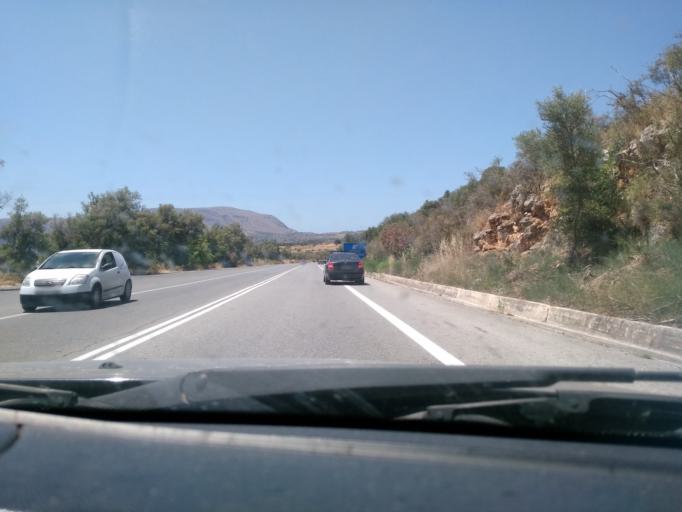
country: GR
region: Crete
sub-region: Nomos Chanias
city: Kalivai
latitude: 35.4287
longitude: 24.1688
